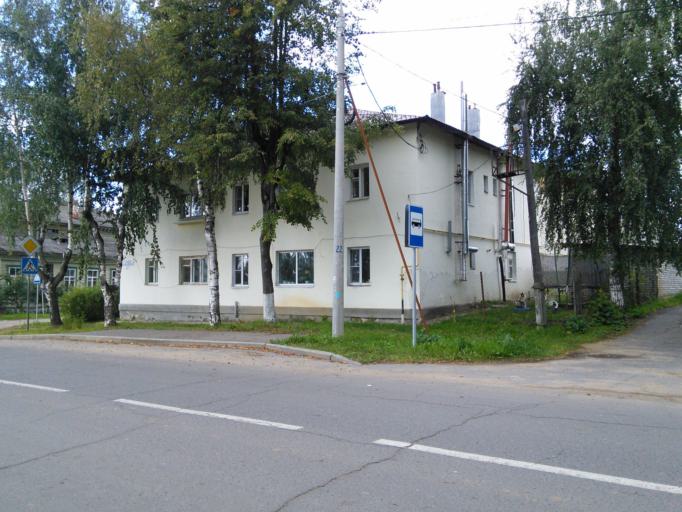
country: RU
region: Jaroslavl
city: Myshkin
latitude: 57.7866
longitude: 38.4525
